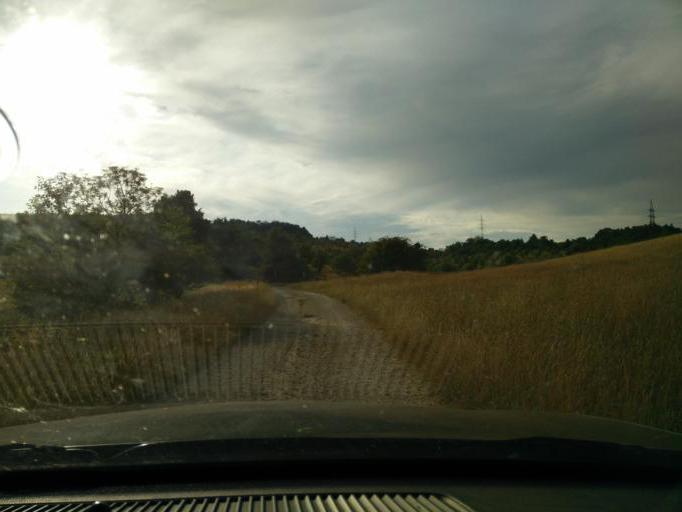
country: HU
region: Fejer
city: Szarliget
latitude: 47.5159
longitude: 18.4666
